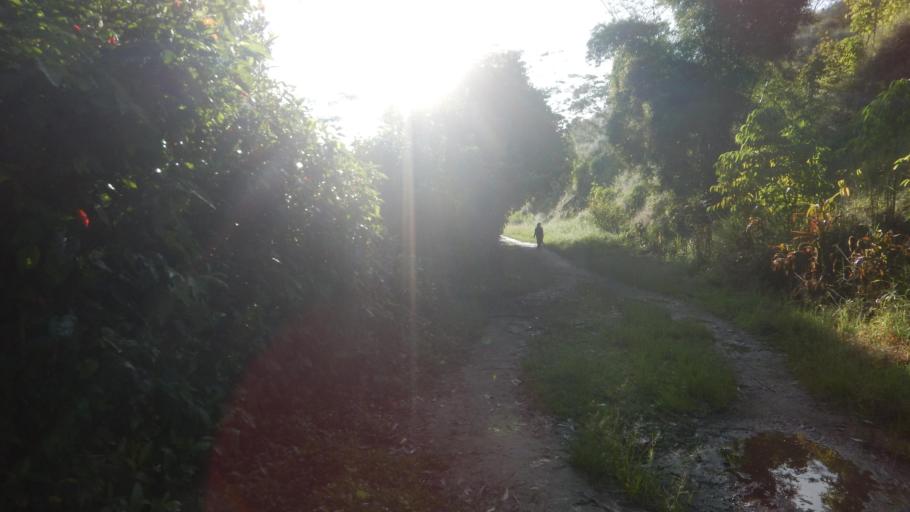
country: PG
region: Western Highlands
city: Rauna
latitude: -5.8002
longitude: 144.3606
